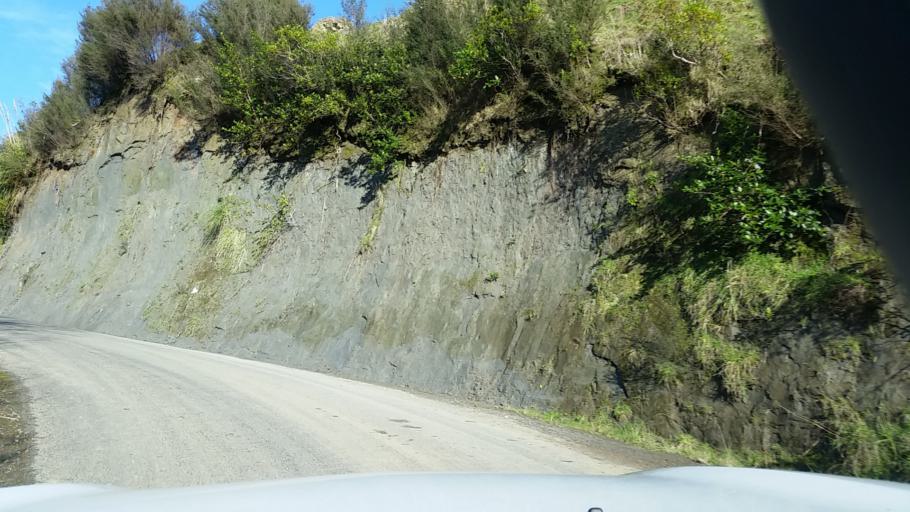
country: NZ
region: Taranaki
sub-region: South Taranaki District
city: Eltham
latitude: -39.5116
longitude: 174.3894
